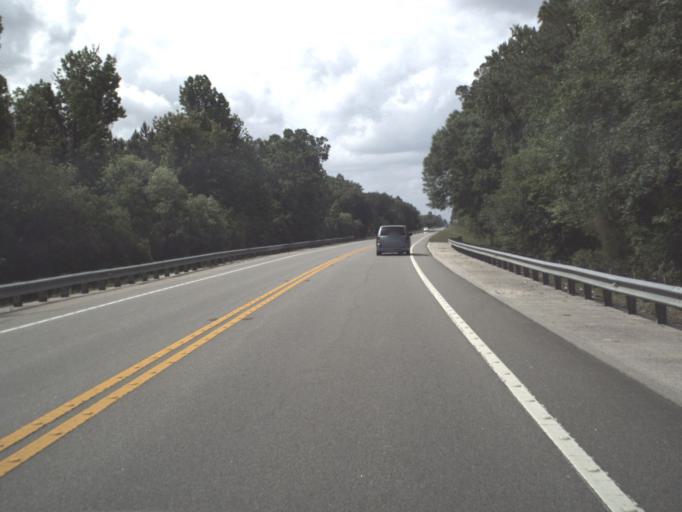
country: US
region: Florida
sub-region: Putnam County
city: Crescent City
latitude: 29.5136
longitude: -81.5000
